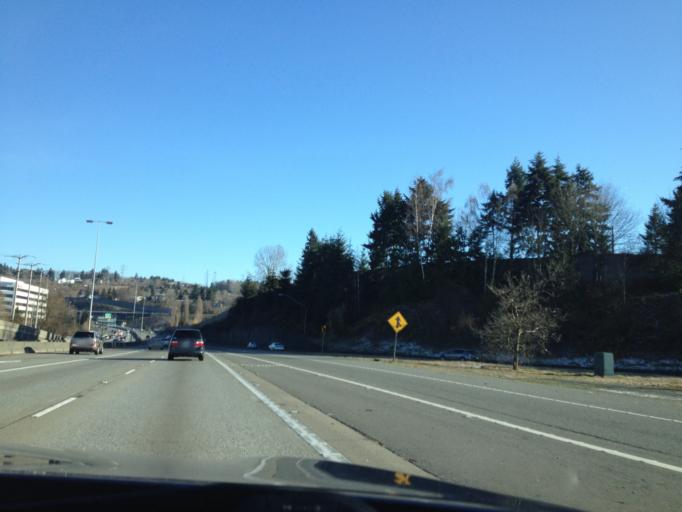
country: US
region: Washington
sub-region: King County
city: Renton
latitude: 47.4677
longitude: -122.2165
